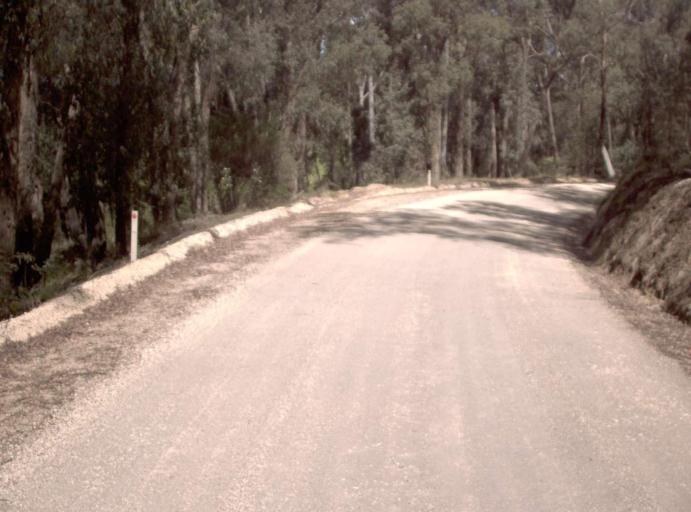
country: AU
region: New South Wales
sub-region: Bombala
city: Bombala
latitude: -37.1808
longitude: 148.7146
